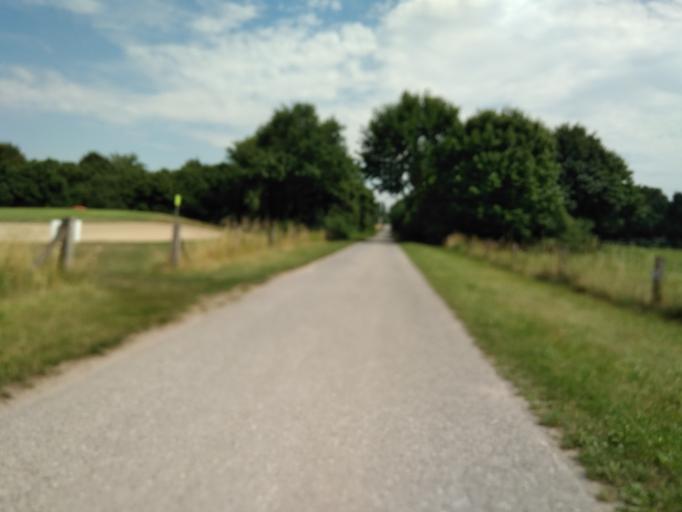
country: DE
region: North Rhine-Westphalia
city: Dorsten
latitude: 51.6322
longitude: 6.9180
